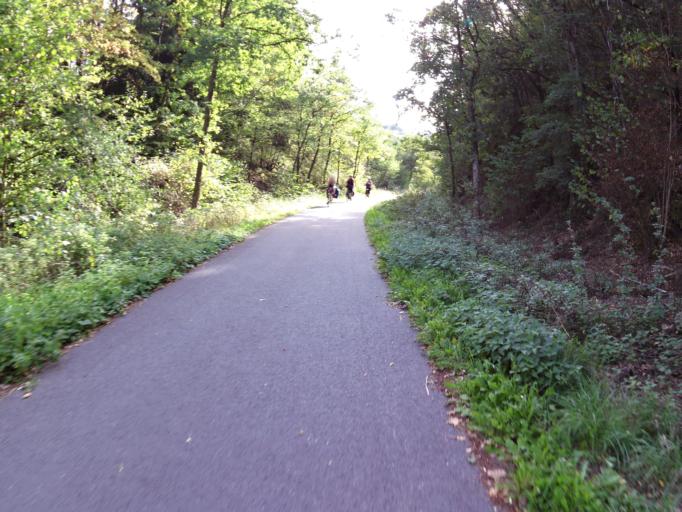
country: DE
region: Rheinland-Pfalz
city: Winterspelt
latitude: 50.2331
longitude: 6.1728
